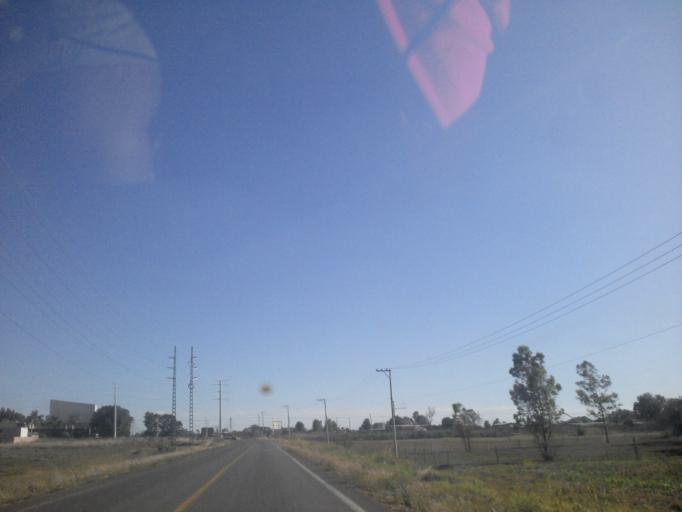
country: MX
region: Jalisco
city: Arandas
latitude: 20.7098
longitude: -102.3768
